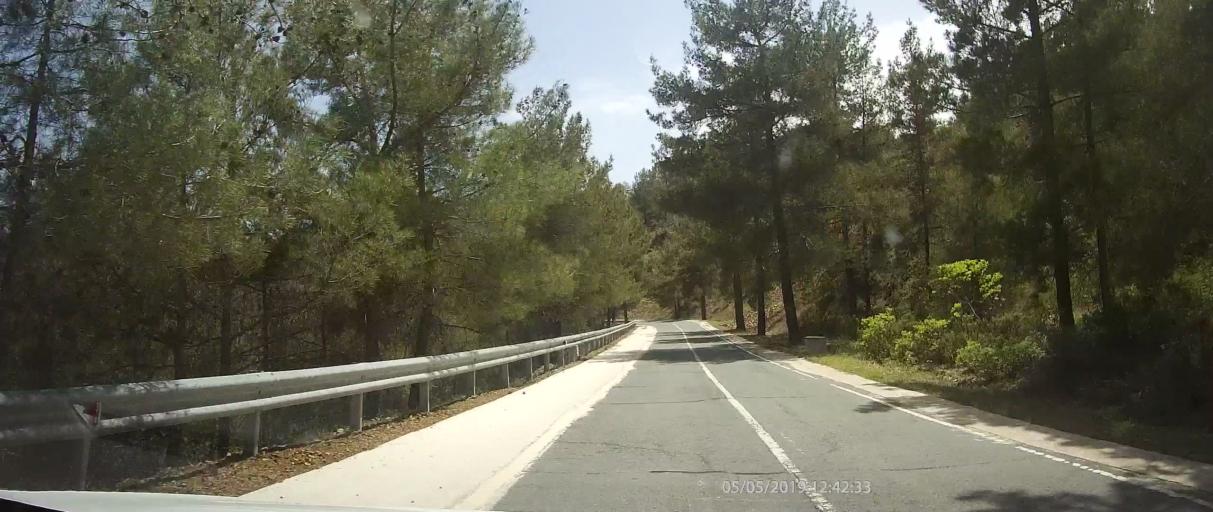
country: CY
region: Lefkosia
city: Kakopetria
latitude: 34.9733
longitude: 32.8110
